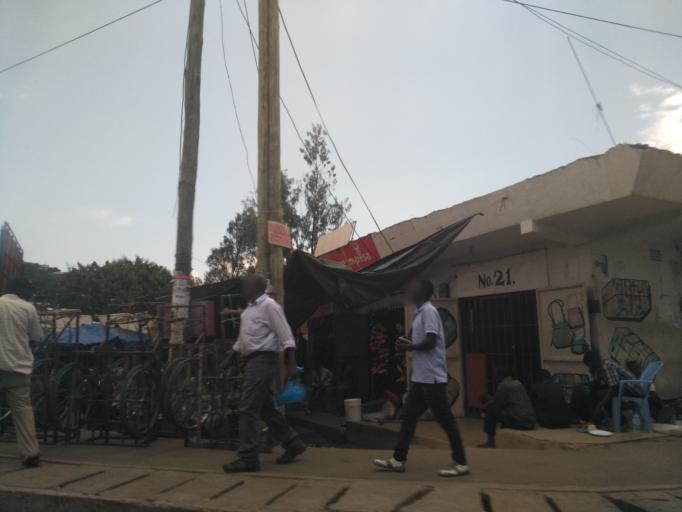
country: TZ
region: Mwanza
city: Mwanza
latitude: -2.5226
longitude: 32.9115
